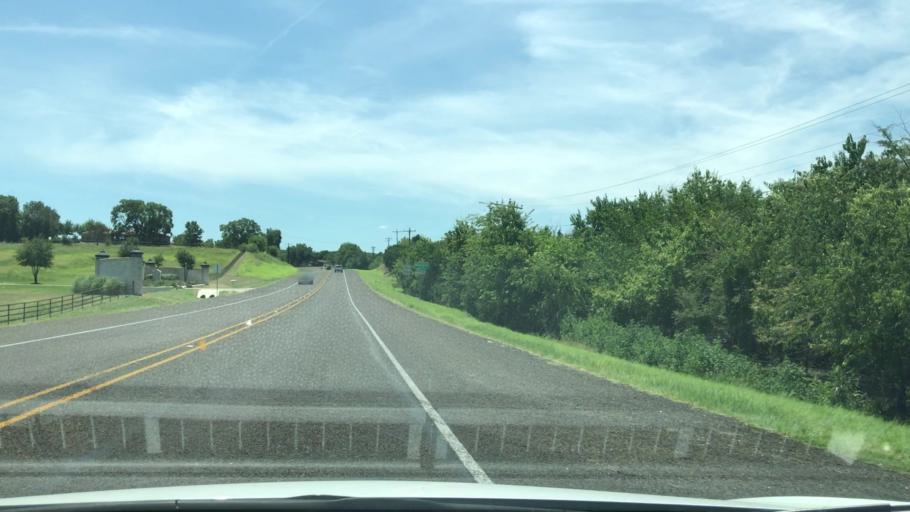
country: US
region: Texas
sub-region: Rockwall County
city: Rockwall
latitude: 32.9774
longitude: -96.4667
